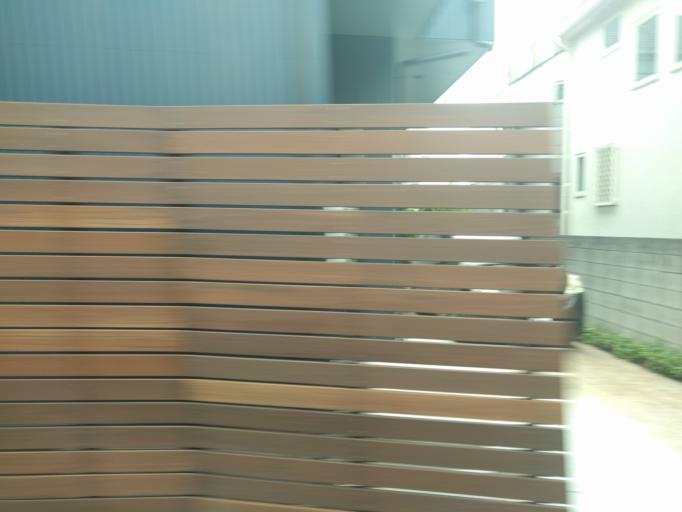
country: JP
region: Tokyo
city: Tokyo
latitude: 35.6341
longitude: 139.7016
